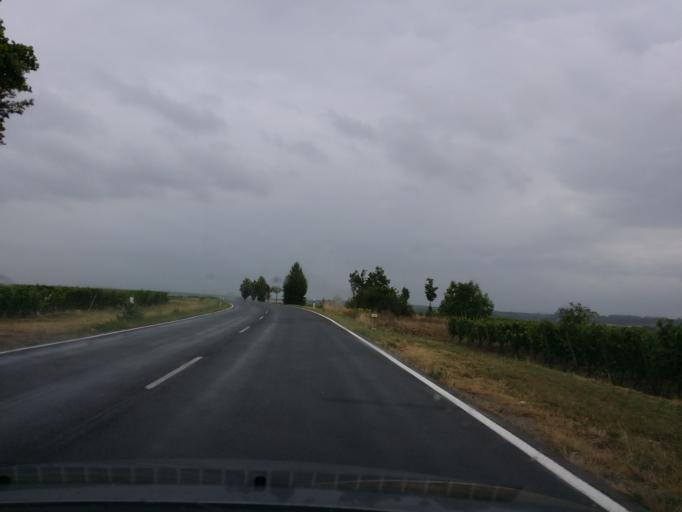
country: DE
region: Rheinland-Pfalz
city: Friesenheim
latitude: 49.8416
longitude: 8.2606
